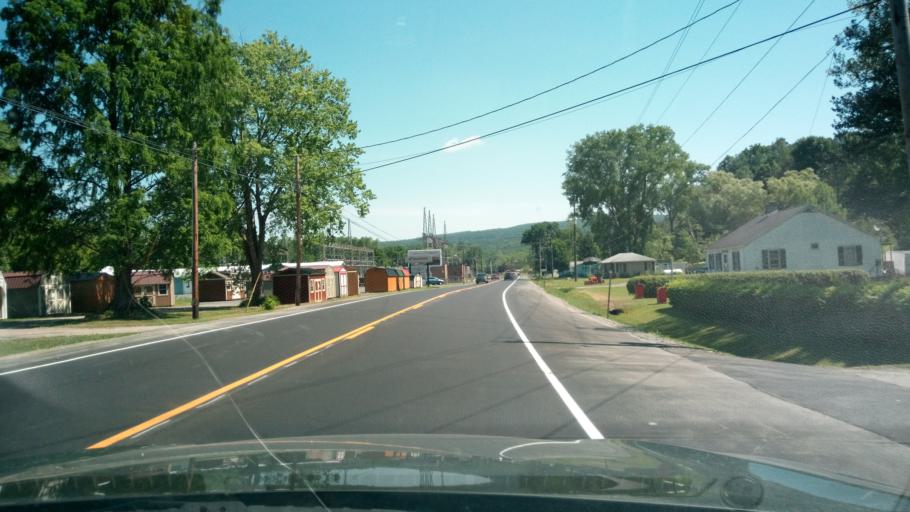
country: US
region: New York
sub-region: Schuyler County
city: Montour Falls
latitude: 42.3257
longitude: -76.8438
